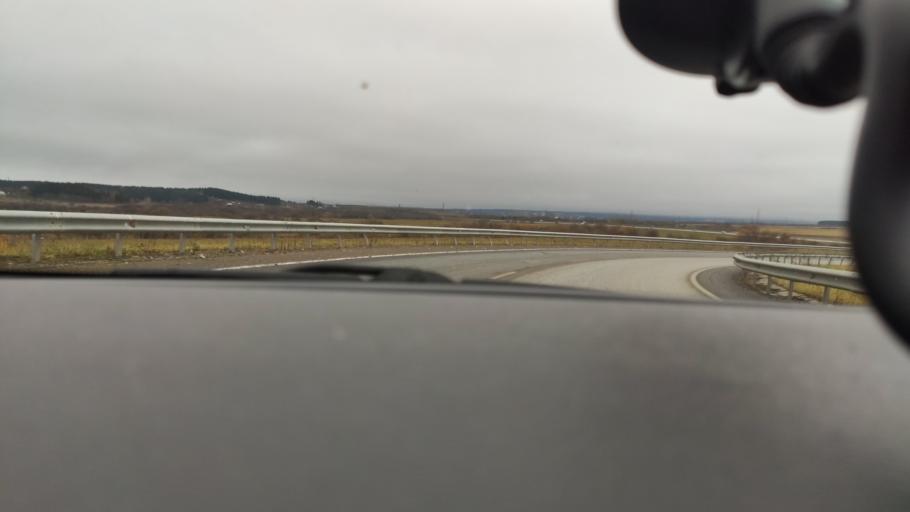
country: RU
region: Perm
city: Kondratovo
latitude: 57.9304
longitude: 56.1754
